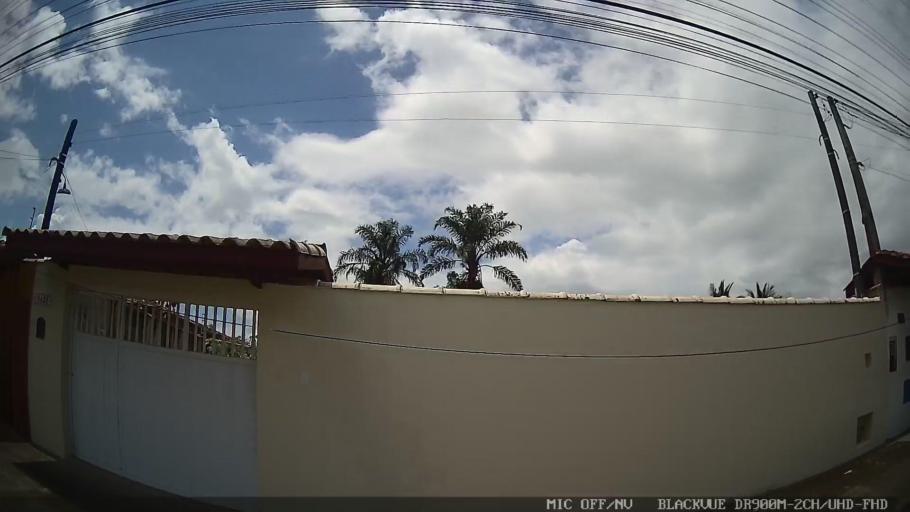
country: BR
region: Sao Paulo
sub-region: Caraguatatuba
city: Caraguatatuba
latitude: -23.6567
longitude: -45.4316
